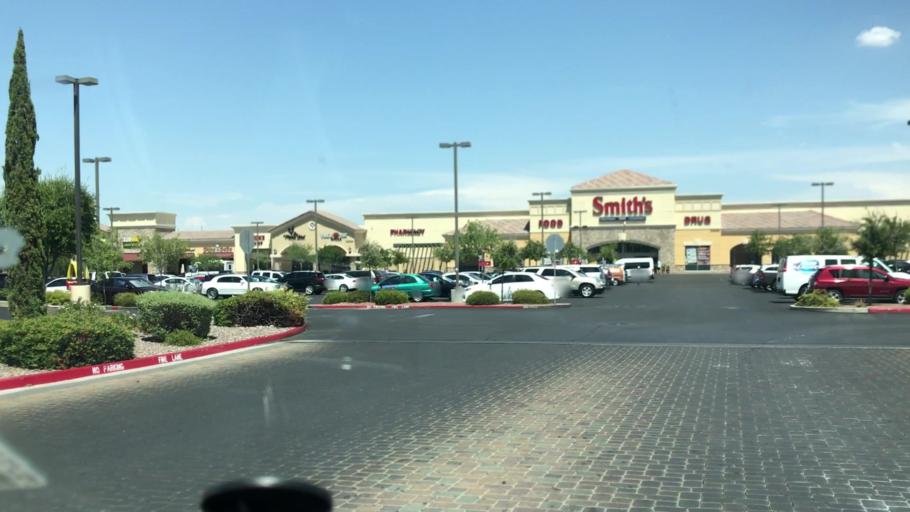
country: US
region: Nevada
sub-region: Clark County
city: Enterprise
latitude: 35.9970
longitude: -115.2071
